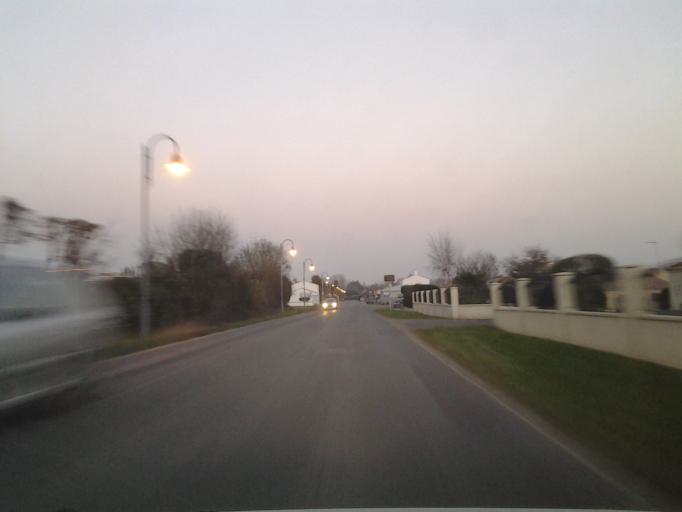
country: FR
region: Pays de la Loire
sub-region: Departement de la Vendee
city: Saint-Gervais
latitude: 46.9034
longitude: -2.0110
